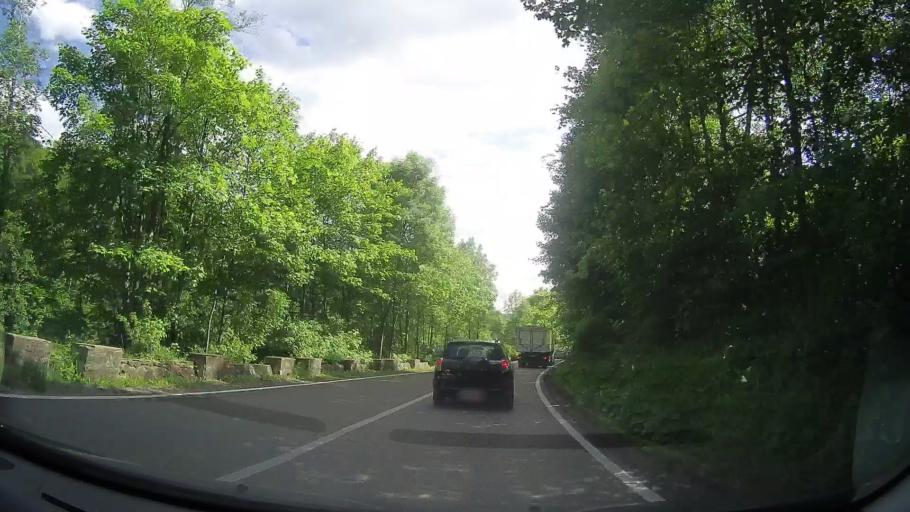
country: RO
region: Prahova
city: Maneciu
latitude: 45.3944
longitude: 25.9321
